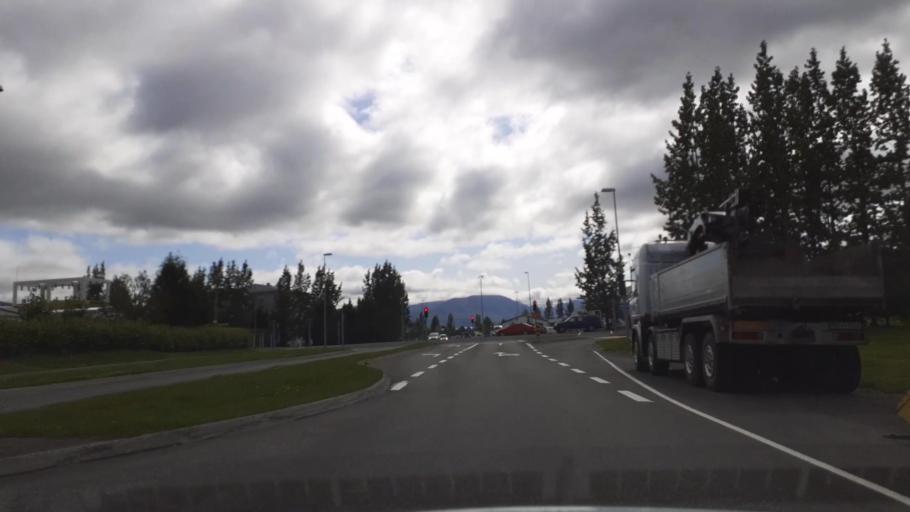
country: IS
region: Northeast
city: Akureyri
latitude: 65.6790
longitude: -18.1152
